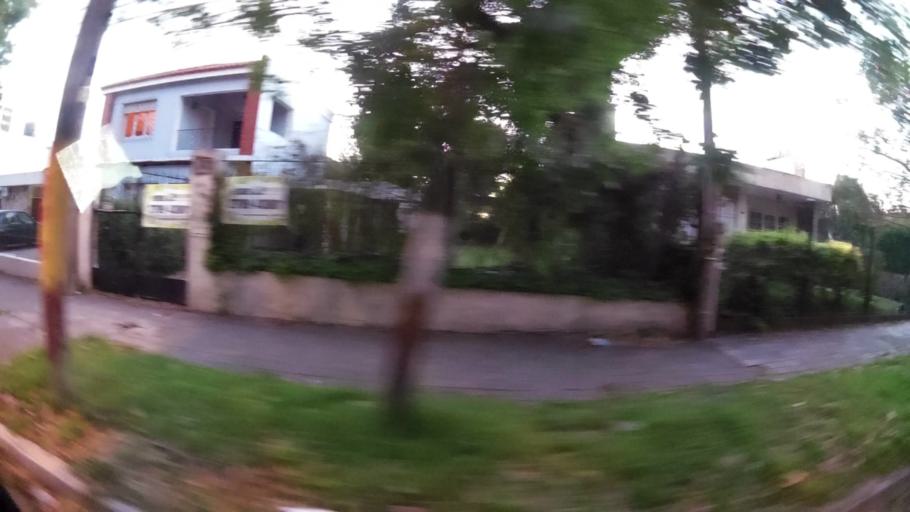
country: UY
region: Canelones
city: Paso de Carrasco
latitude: -34.8843
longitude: -56.0963
